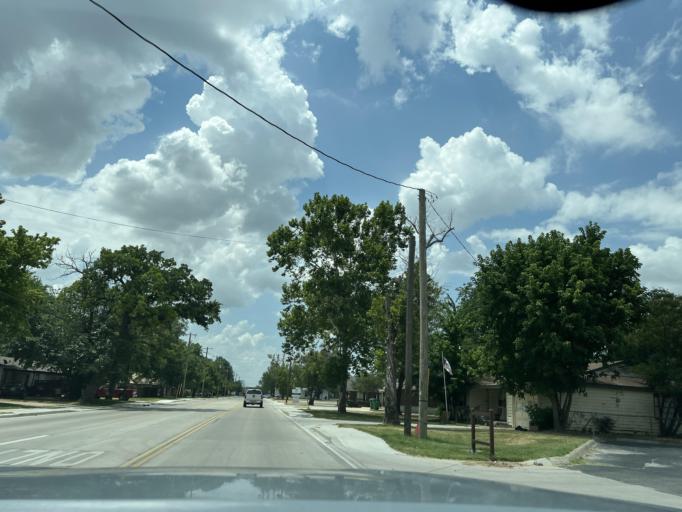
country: US
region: Texas
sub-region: Parker County
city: Springtown
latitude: 32.9705
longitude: -97.6848
